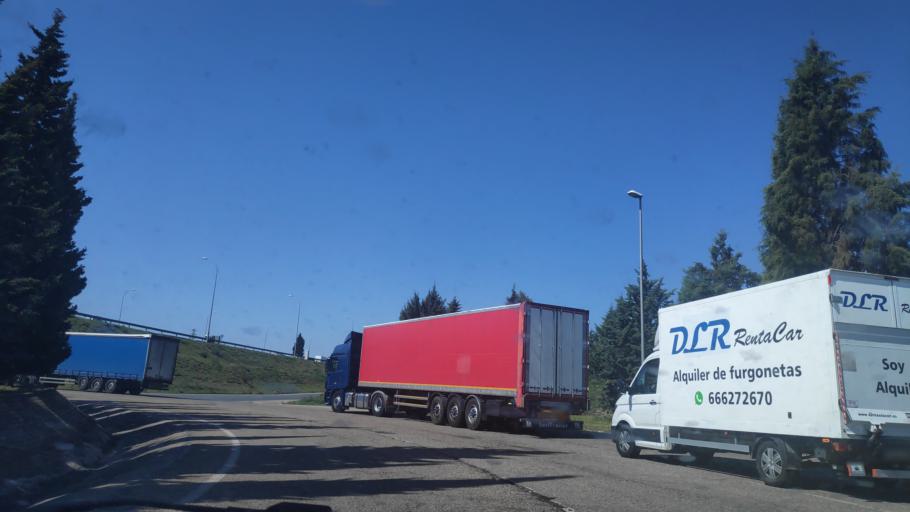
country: ES
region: Madrid
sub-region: Provincia de Madrid
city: Pinto
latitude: 40.2742
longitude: -3.7007
